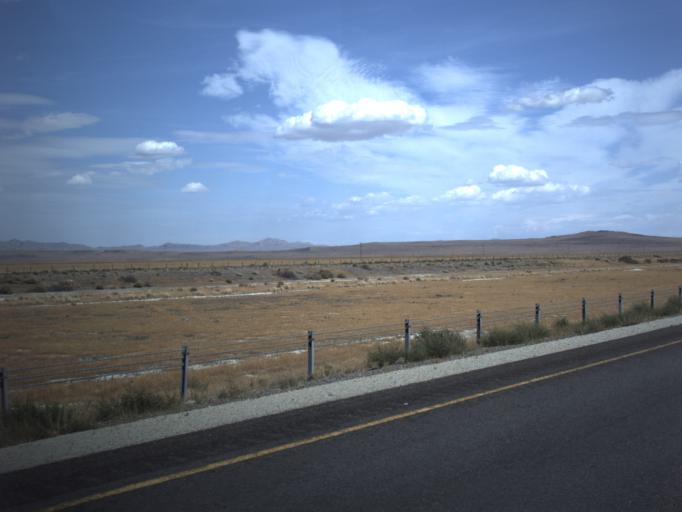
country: US
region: Utah
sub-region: Tooele County
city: Grantsville
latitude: 40.7261
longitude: -113.2252
